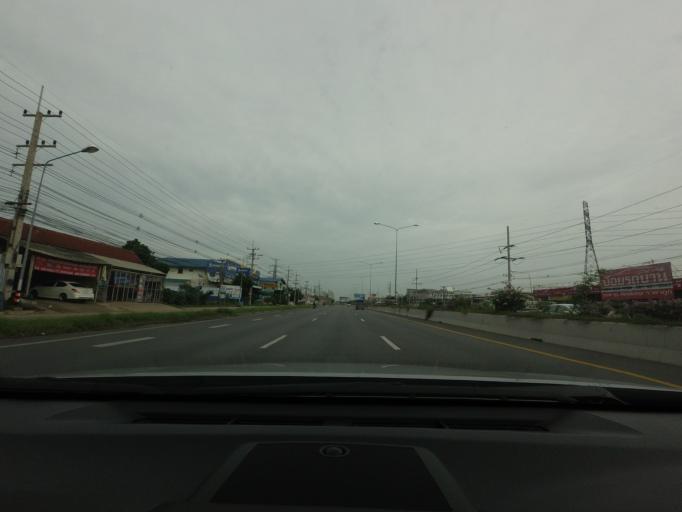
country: TH
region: Phetchaburi
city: Phetchaburi
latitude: 13.0924
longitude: 99.9405
